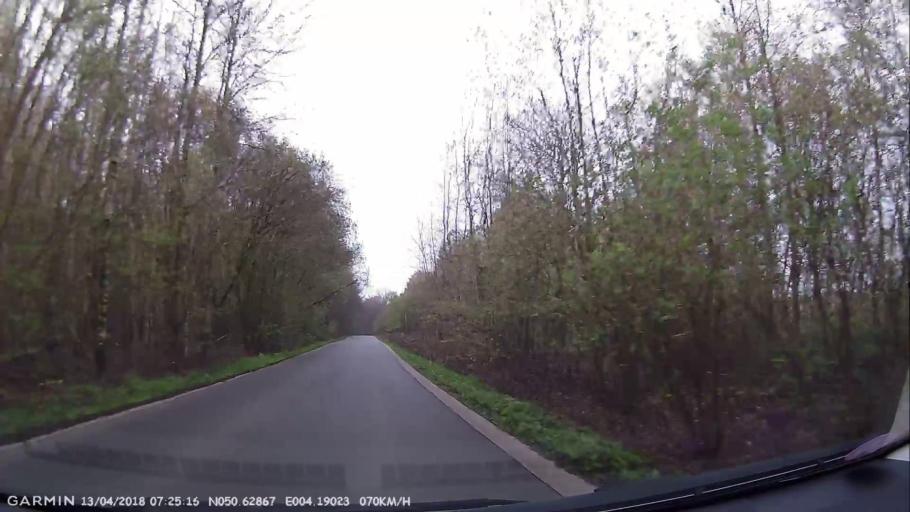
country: BE
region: Wallonia
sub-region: Province du Hainaut
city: Braine-le-Comte
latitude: 50.6284
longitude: 4.1900
